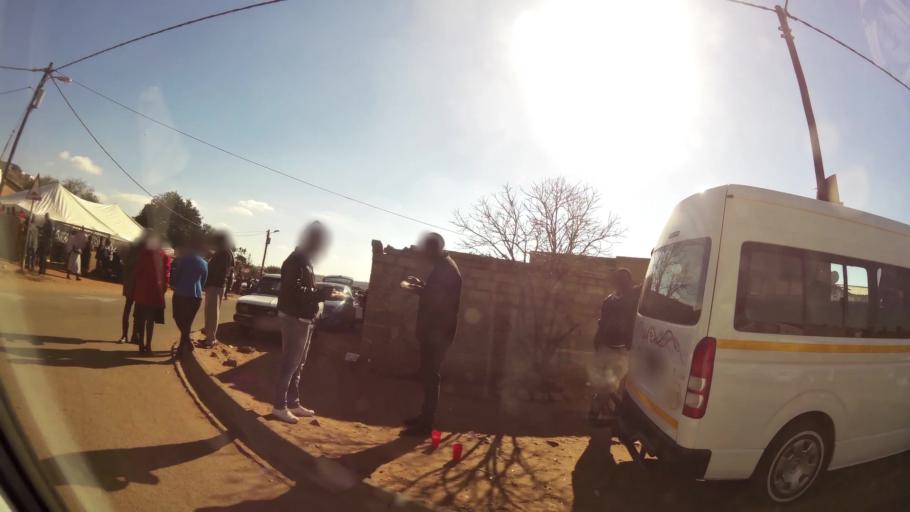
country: ZA
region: Gauteng
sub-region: City of Tshwane Metropolitan Municipality
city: Cullinan
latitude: -25.6950
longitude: 28.4167
